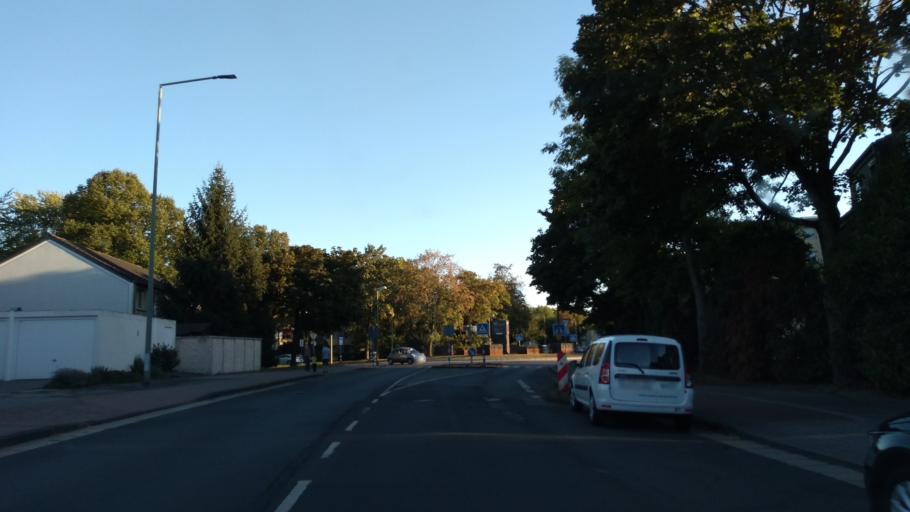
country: DE
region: North Rhine-Westphalia
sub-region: Regierungsbezirk Dusseldorf
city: Dinslaken
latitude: 51.5444
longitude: 6.7154
